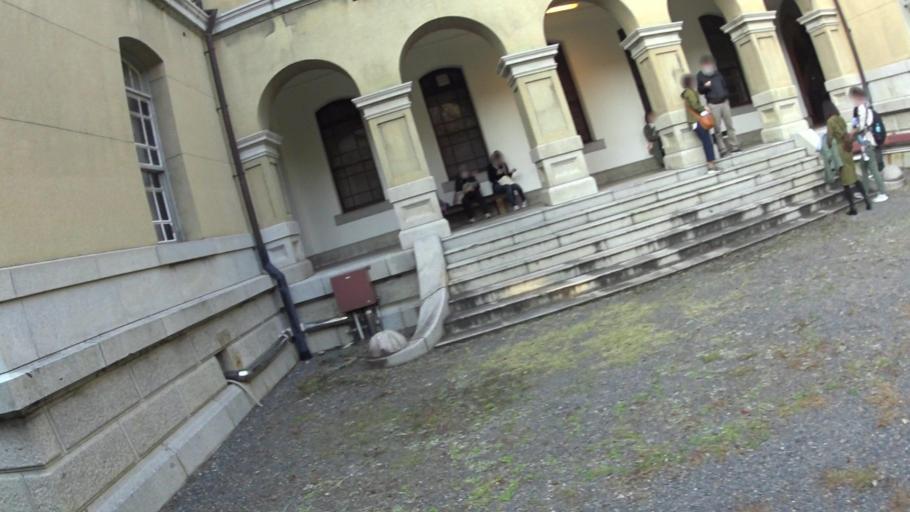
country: JP
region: Kyoto
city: Kyoto
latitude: 35.0210
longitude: 135.7556
